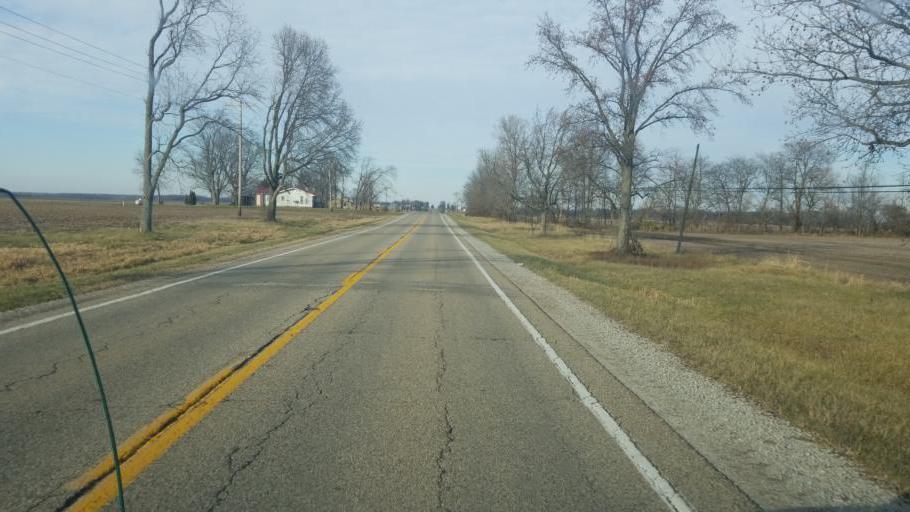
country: US
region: Illinois
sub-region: Lawrence County
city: Bridgeport
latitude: 38.5964
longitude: -87.6943
